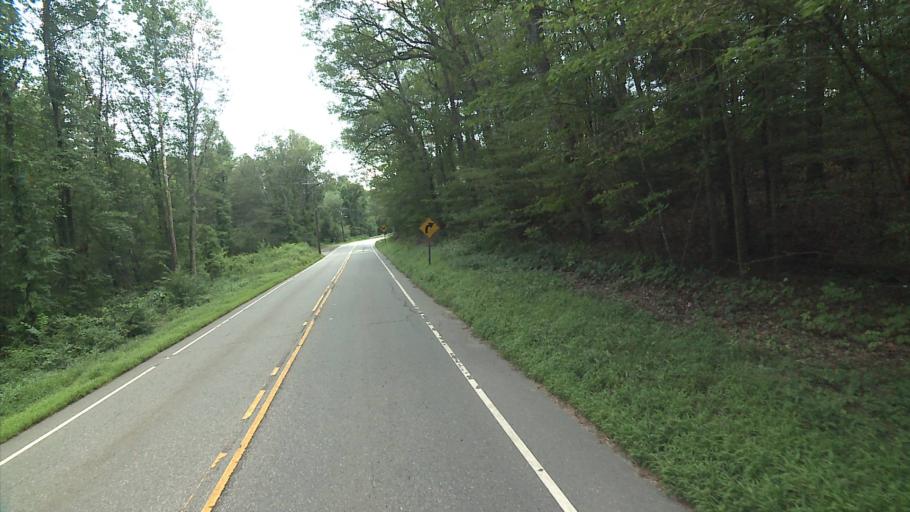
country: US
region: Connecticut
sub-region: Windham County
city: South Windham
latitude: 41.6843
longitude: -72.1644
